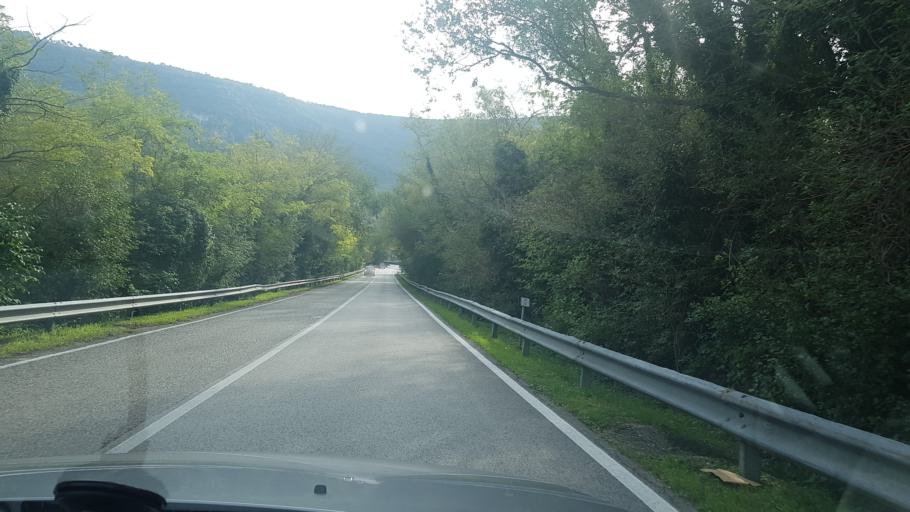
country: IT
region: Friuli Venezia Giulia
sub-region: Provincia di Trieste
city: Dolina
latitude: 45.6044
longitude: 13.8522
